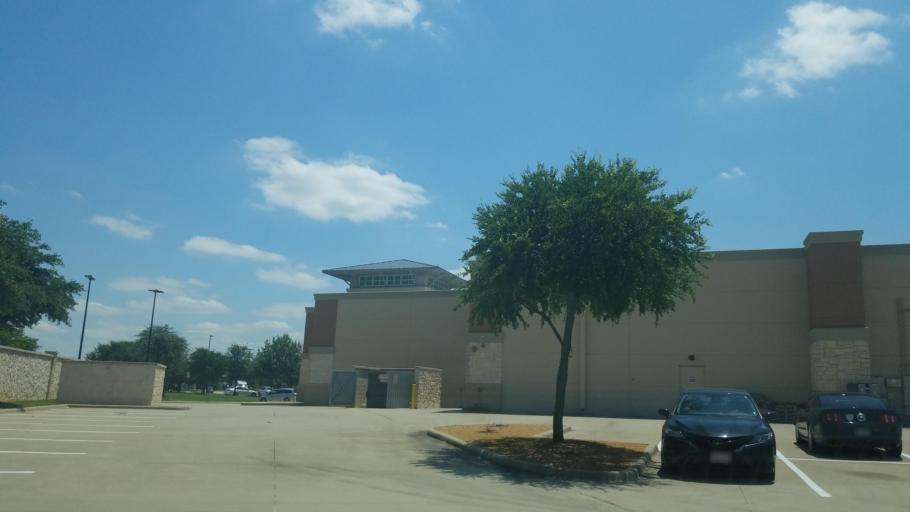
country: US
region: Texas
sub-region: Denton County
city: Copper Canyon
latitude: 33.0771
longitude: -97.0795
